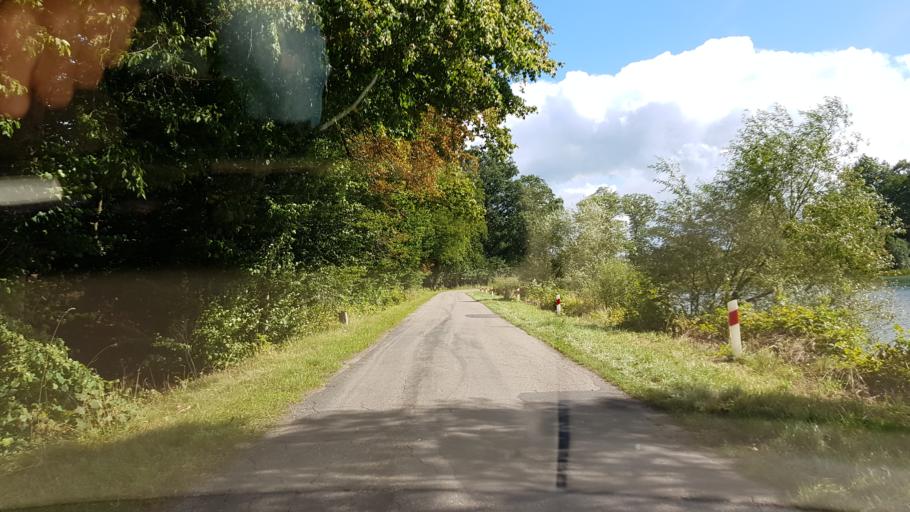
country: PL
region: West Pomeranian Voivodeship
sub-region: Powiat bialogardzki
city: Tychowo
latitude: 53.9819
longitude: 16.3094
